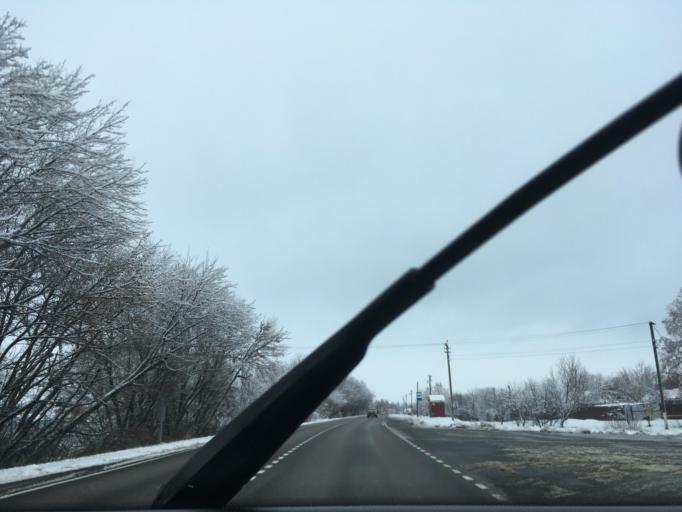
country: RU
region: Voronezj
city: Zabolotovka
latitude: 50.2470
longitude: 39.3552
